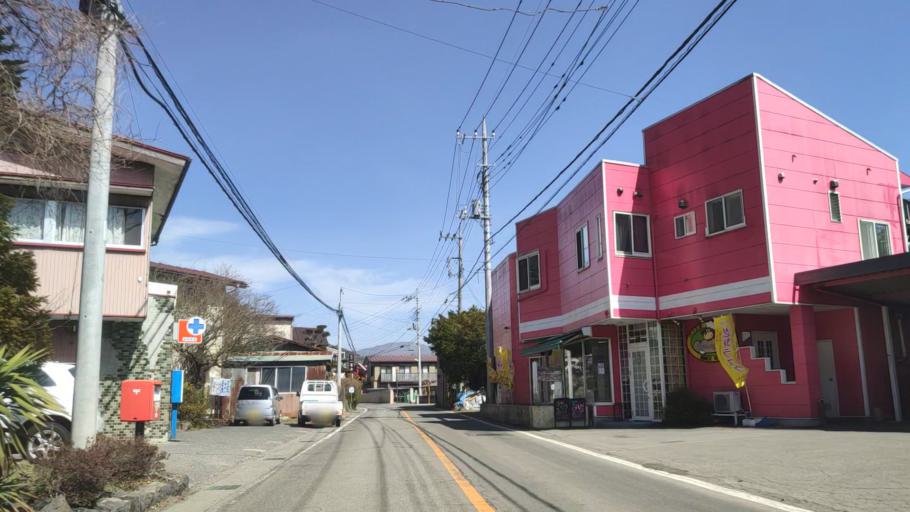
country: JP
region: Yamanashi
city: Fujikawaguchiko
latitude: 35.4585
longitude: 138.8269
